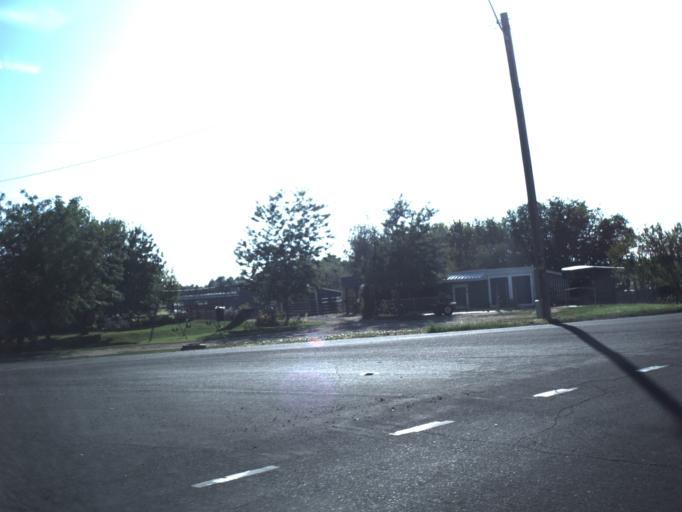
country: US
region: Utah
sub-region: Weber County
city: Hooper
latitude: 41.1399
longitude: -112.1221
